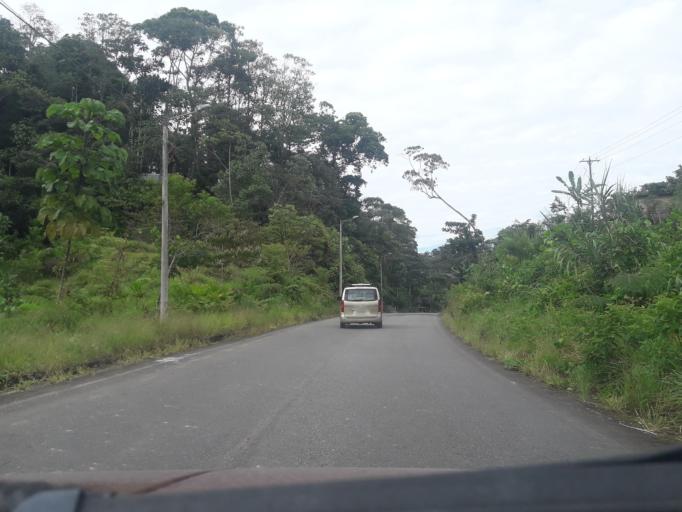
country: EC
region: Napo
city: Tena
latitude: -1.0309
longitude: -77.8880
